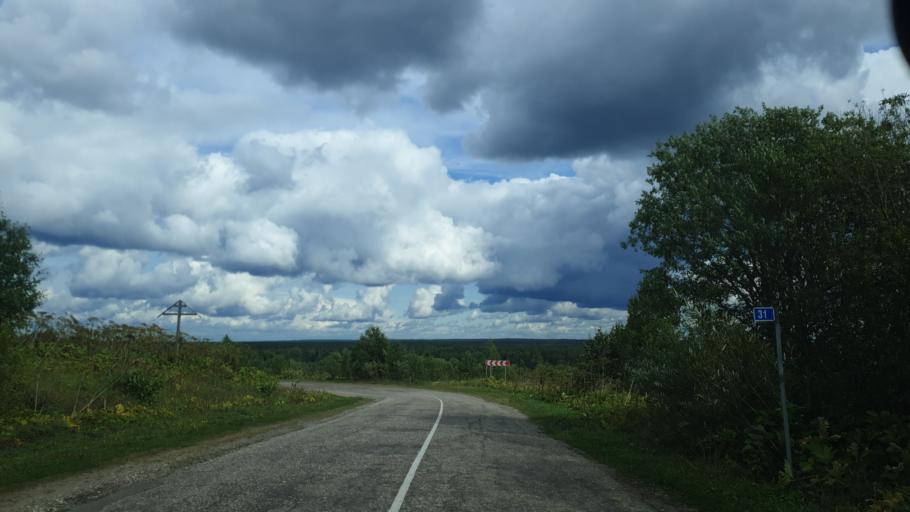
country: RU
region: Komi Republic
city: Aykino
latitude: 61.9582
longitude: 50.1863
